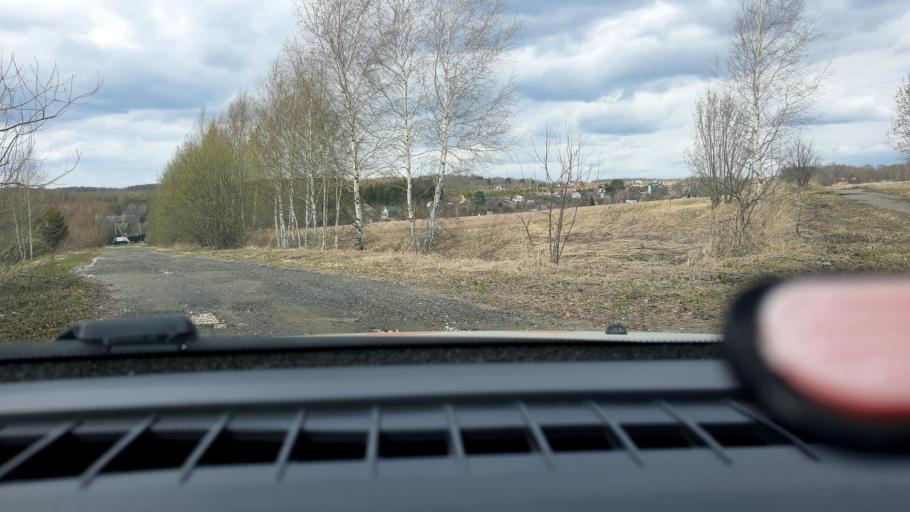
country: RU
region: Nizjnij Novgorod
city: Babino
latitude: 56.1708
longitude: 43.6768
